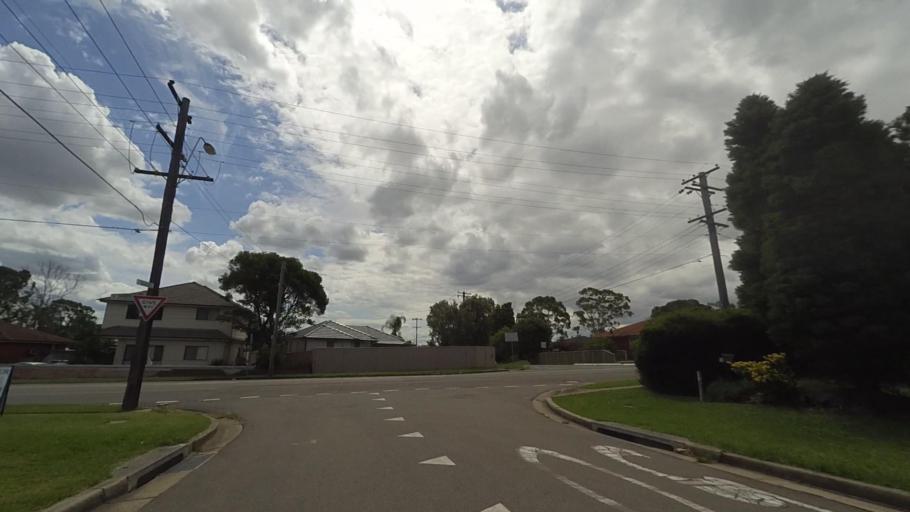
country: AU
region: New South Wales
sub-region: Holroyd
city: Guildford West
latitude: -33.8470
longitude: 150.9623
